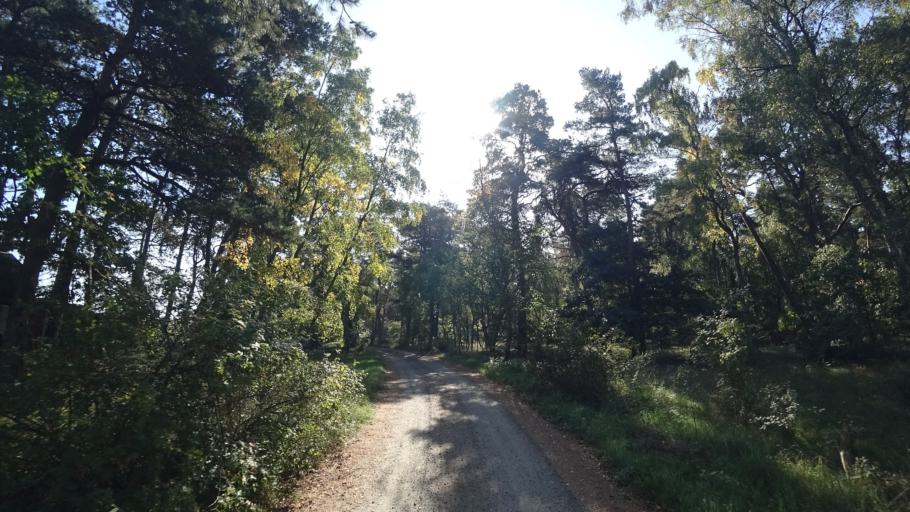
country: SE
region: Skane
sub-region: Kristianstads Kommun
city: Ahus
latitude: 55.9260
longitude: 14.3183
